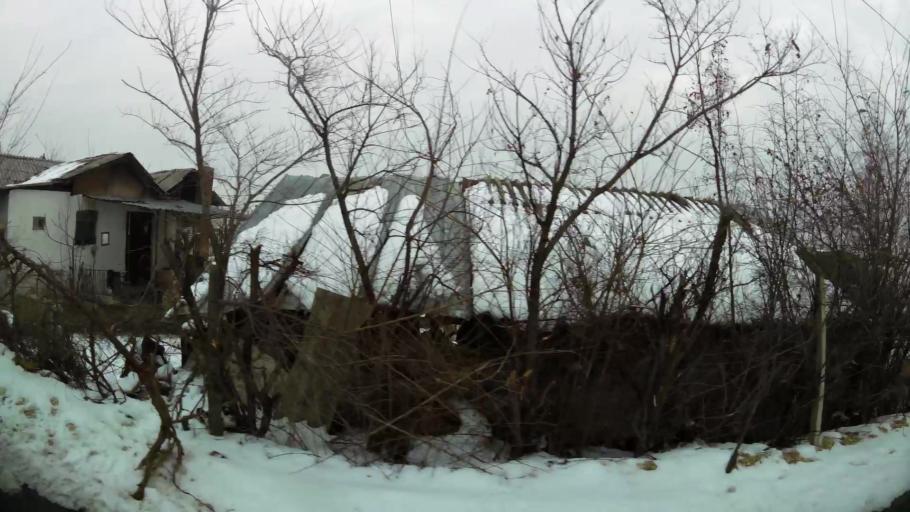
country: MK
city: Kondovo
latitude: 42.0394
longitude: 21.3439
